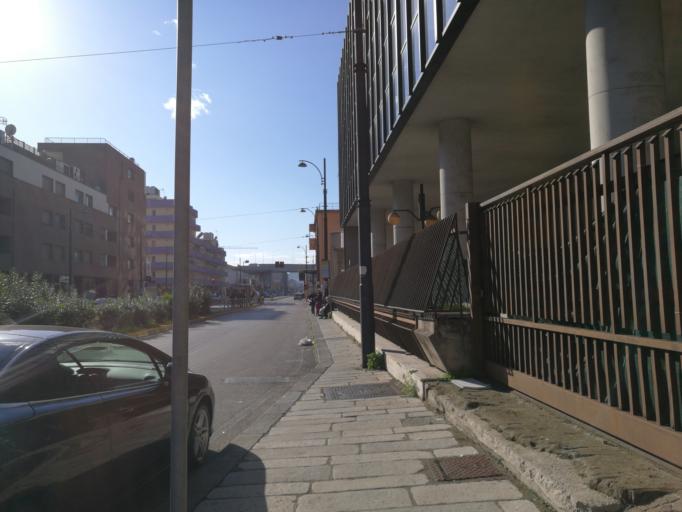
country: IT
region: Campania
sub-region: Provincia di Napoli
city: Casavatore
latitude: 40.8657
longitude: 14.2889
